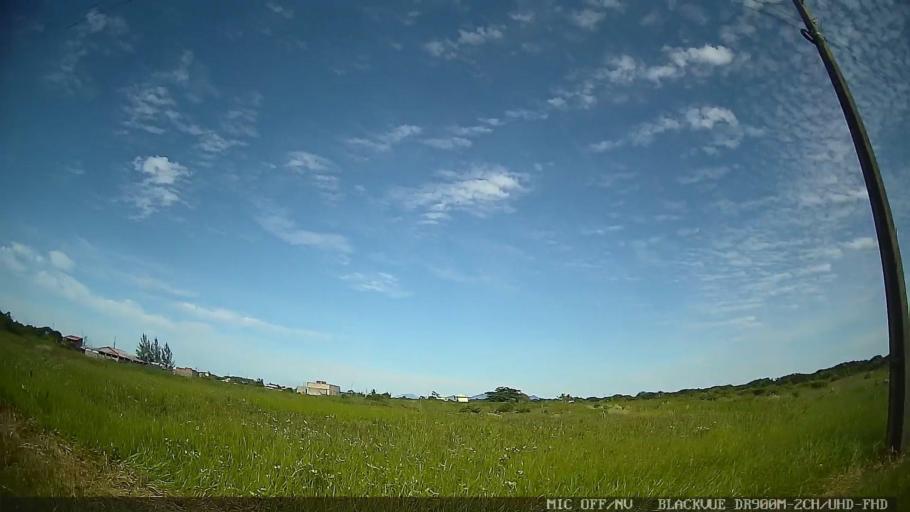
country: BR
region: Sao Paulo
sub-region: Iguape
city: Iguape
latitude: -24.7733
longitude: -47.5931
